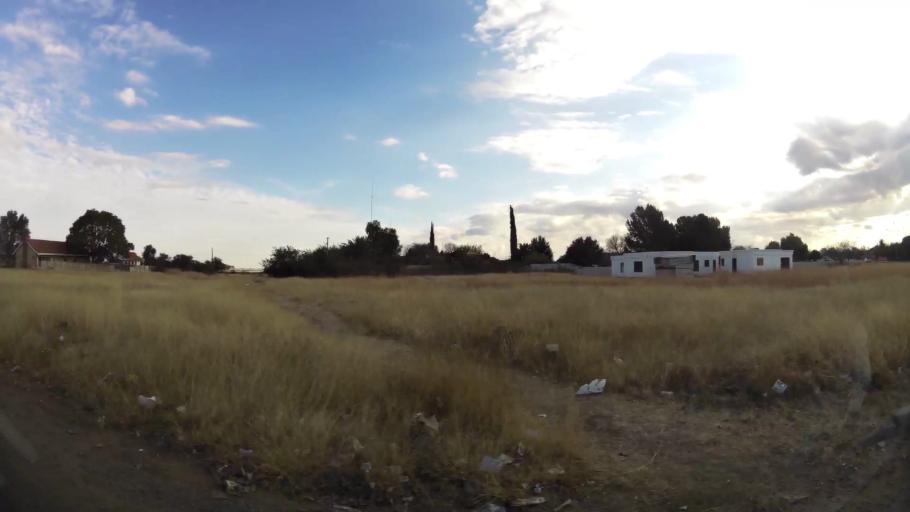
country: ZA
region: Orange Free State
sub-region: Lejweleputswa District Municipality
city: Welkom
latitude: -27.9814
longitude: 26.7008
